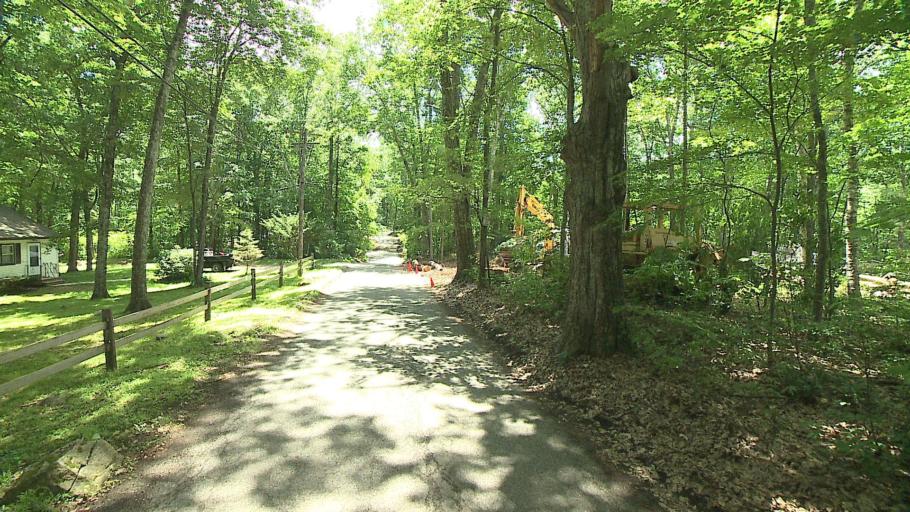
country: US
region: Connecticut
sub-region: Litchfield County
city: New Preston
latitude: 41.6973
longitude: -73.2829
